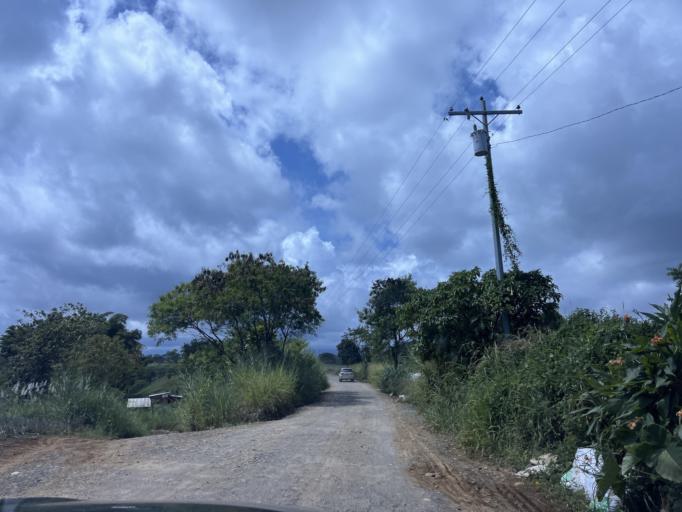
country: PH
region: Northern Mindanao
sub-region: Province of Bukidnon
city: Impalutao
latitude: 8.2464
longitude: 125.0004
